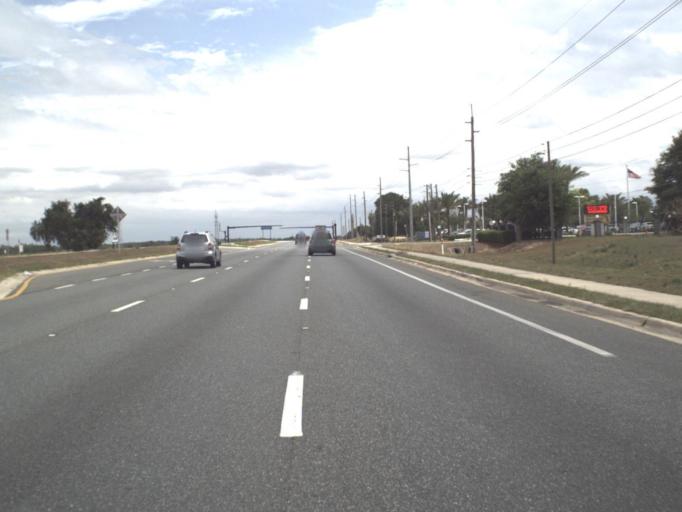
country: US
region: Florida
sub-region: Orange County
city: Oakland
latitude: 28.5463
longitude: -81.6683
